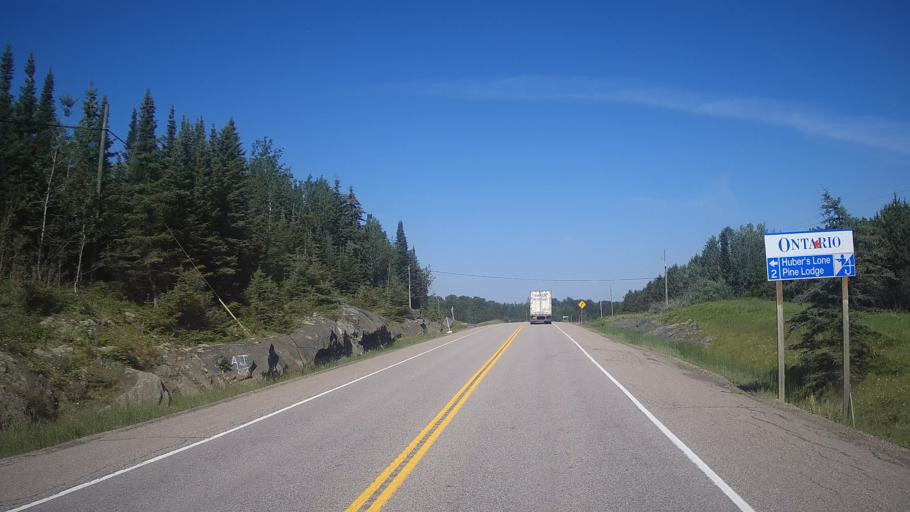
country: CA
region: Ontario
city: Dryden
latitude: 49.6971
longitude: -92.5626
